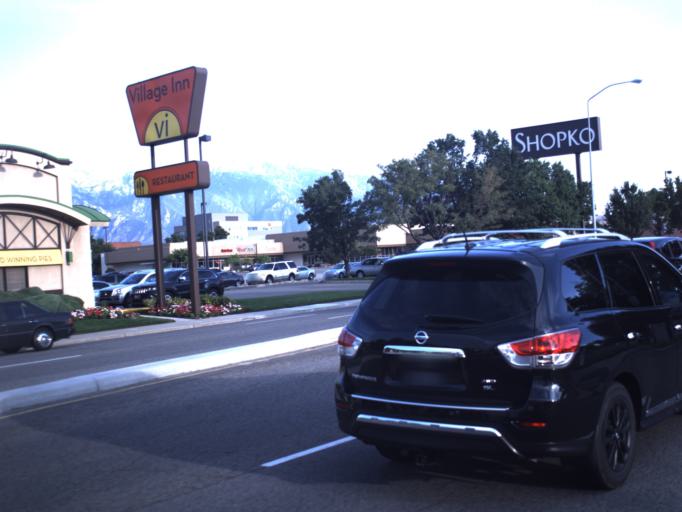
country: US
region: Utah
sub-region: Salt Lake County
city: Murray
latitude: 40.6421
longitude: -111.8891
